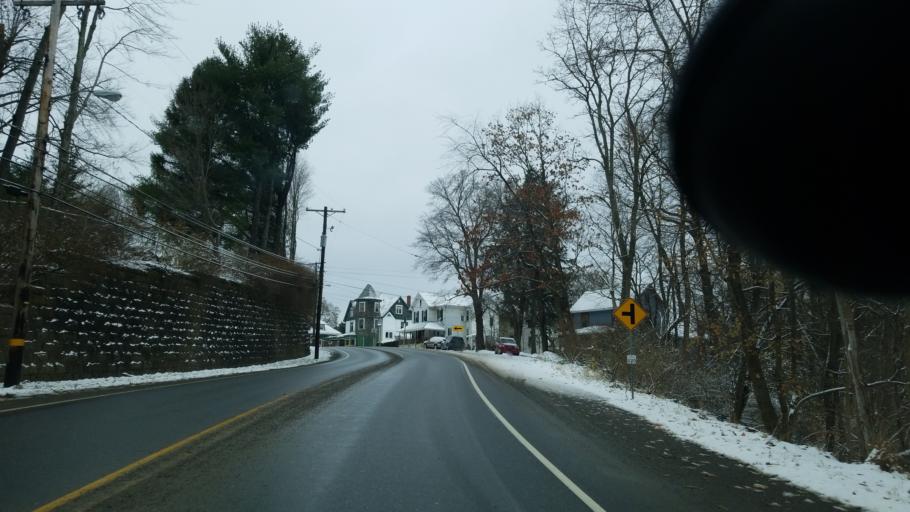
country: US
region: Pennsylvania
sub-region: Jefferson County
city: Punxsutawney
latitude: 40.9431
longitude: -78.9560
